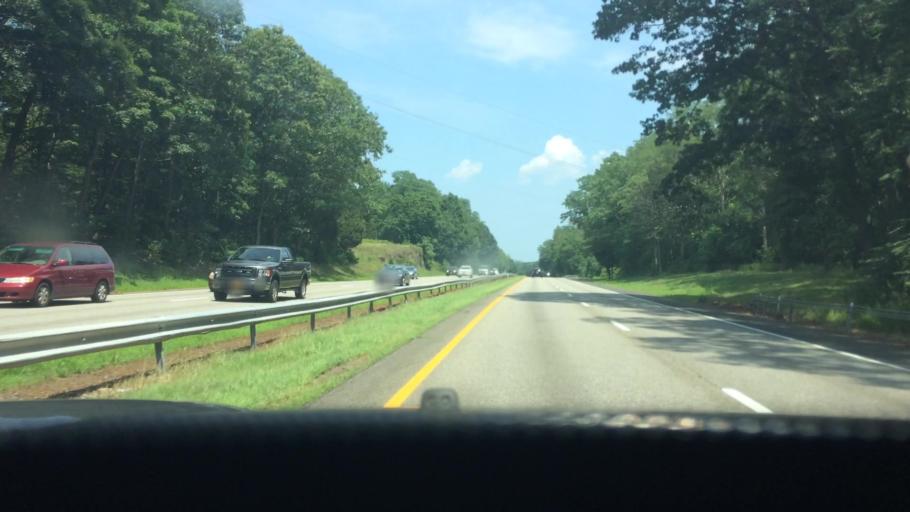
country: US
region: Connecticut
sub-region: New Haven County
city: Wallingford
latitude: 41.4387
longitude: -72.8484
